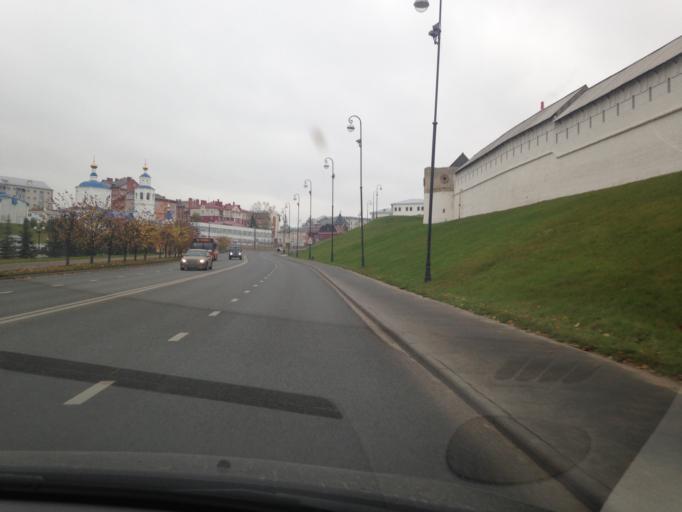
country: RU
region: Tatarstan
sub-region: Gorod Kazan'
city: Kazan
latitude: 55.8011
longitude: 49.1077
